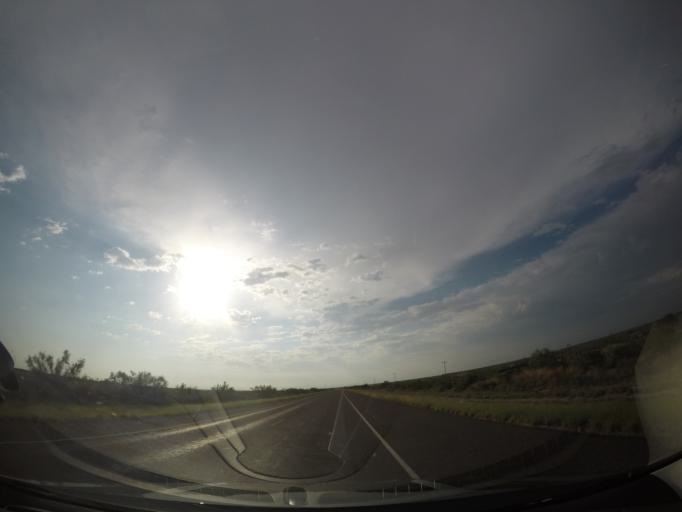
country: US
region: Texas
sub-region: Terrell County
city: Sanderson
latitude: 30.0488
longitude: -102.1355
